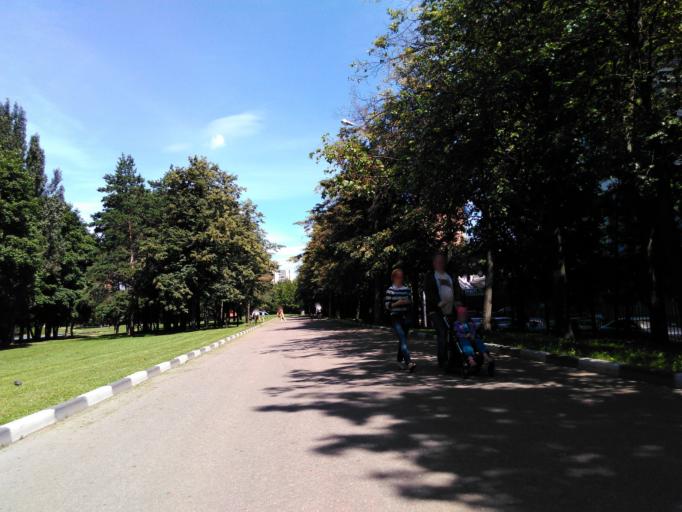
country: RU
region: Moskovskaya
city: Leninskiye Gory
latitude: 55.7026
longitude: 37.5613
